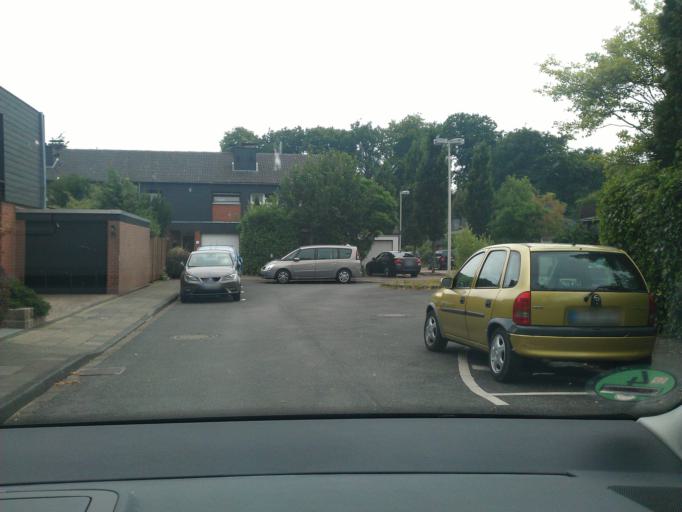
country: DE
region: North Rhine-Westphalia
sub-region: Regierungsbezirk Dusseldorf
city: Hilden
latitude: 51.1623
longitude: 6.9499
